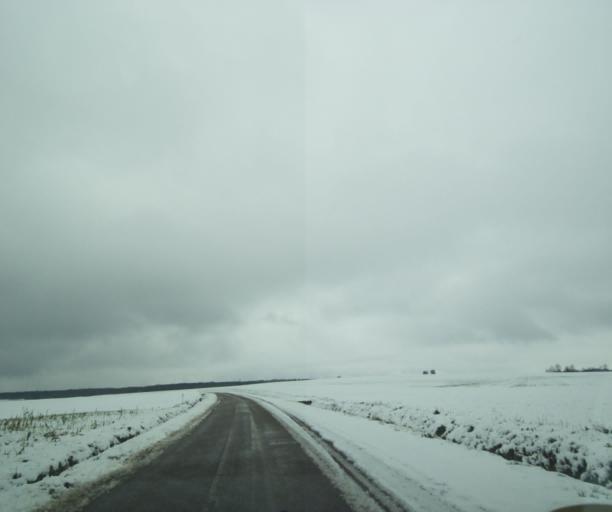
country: FR
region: Champagne-Ardenne
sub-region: Departement de la Haute-Marne
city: Laneuville-a-Remy
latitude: 48.4035
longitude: 4.8533
